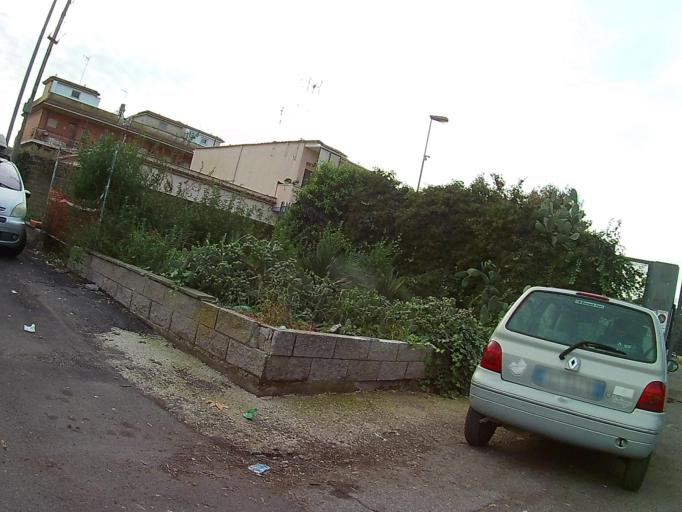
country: IT
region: Latium
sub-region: Citta metropolitana di Roma Capitale
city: Lido di Ostia
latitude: 41.7415
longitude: 12.2883
